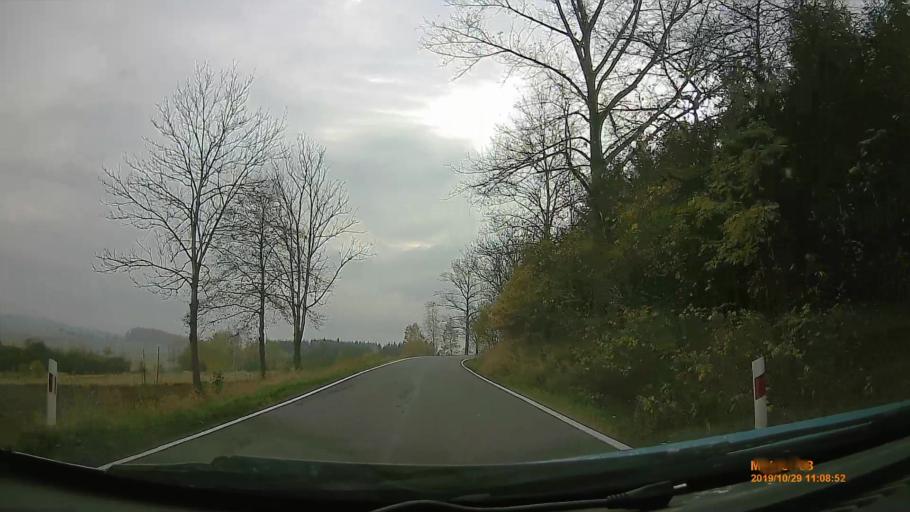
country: PL
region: Lower Silesian Voivodeship
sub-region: Powiat klodzki
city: Polanica-Zdroj
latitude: 50.4484
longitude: 16.4953
